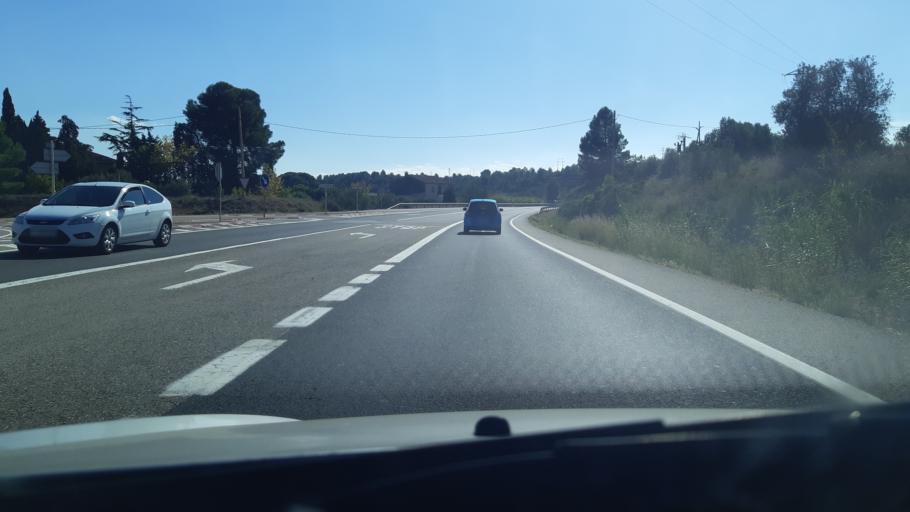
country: ES
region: Catalonia
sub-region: Provincia de Tarragona
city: Tivenys
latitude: 40.9050
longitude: 0.4833
